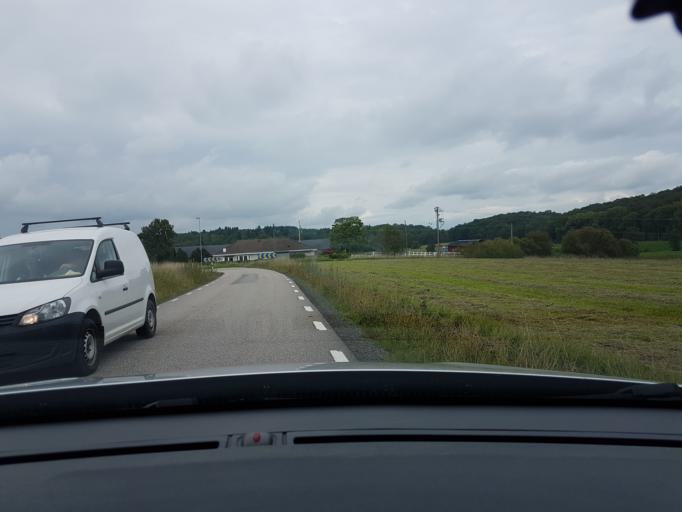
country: SE
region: Vaestra Goetaland
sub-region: Ale Kommun
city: Alvangen
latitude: 57.9275
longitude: 12.1326
